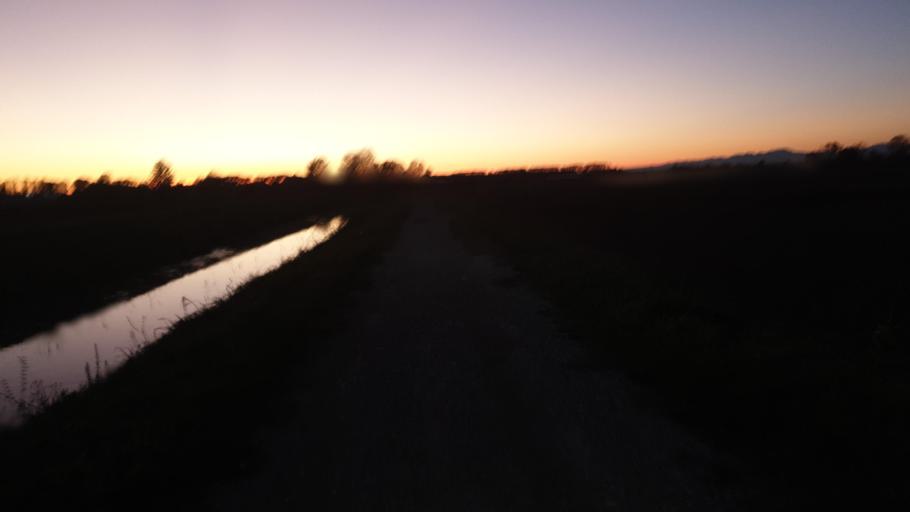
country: IT
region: Veneto
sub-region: Provincia di Venezia
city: Fiesso d'Artico
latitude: 45.4274
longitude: 12.0276
